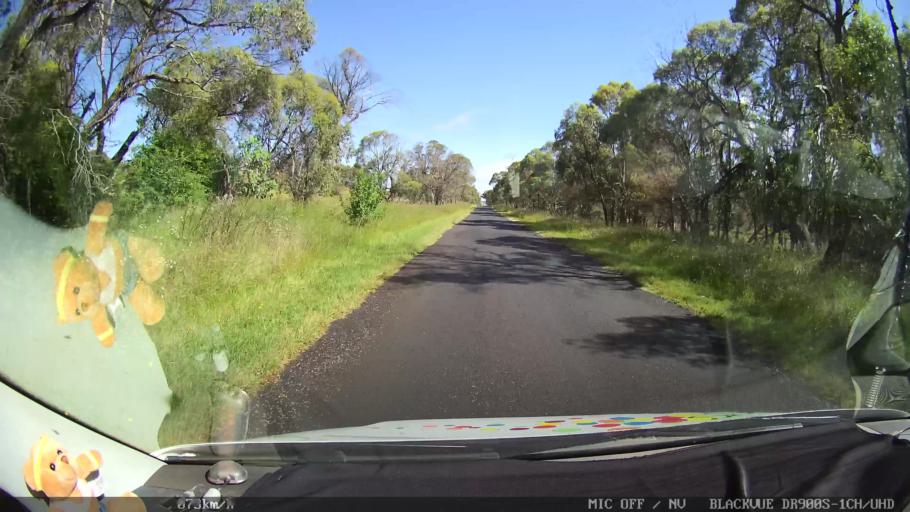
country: AU
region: New South Wales
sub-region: Guyra
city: Guyra
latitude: -30.0923
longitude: 151.6786
